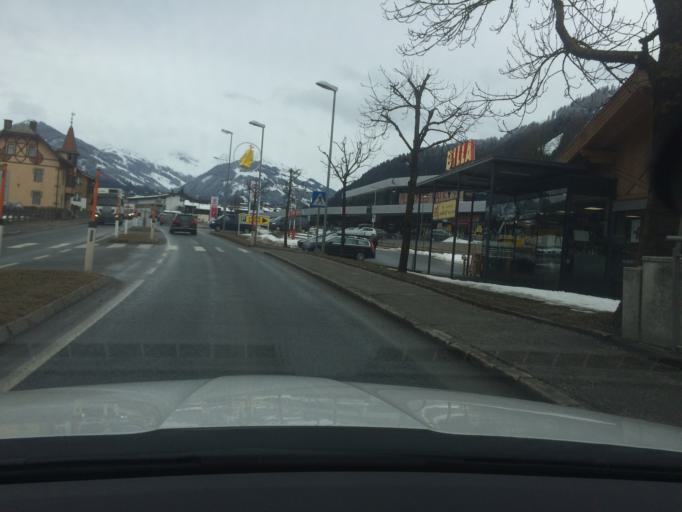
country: AT
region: Tyrol
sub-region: Politischer Bezirk Kitzbuhel
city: Kitzbuhel
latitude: 47.4388
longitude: 12.4003
